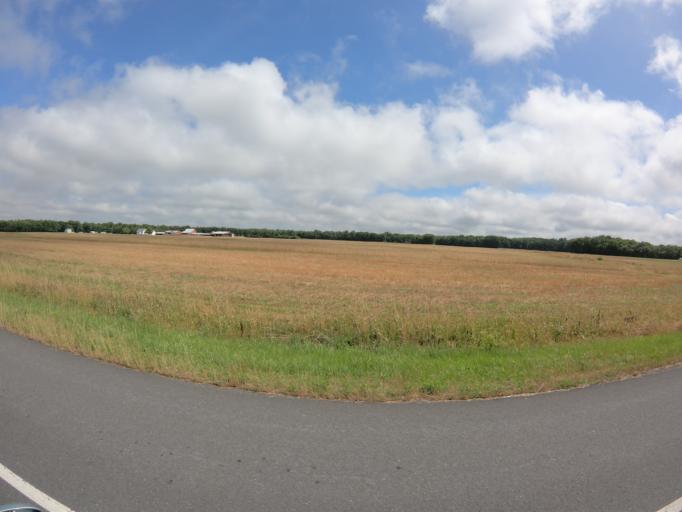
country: US
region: Maryland
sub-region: Caroline County
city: Greensboro
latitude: 39.0464
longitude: -75.8277
